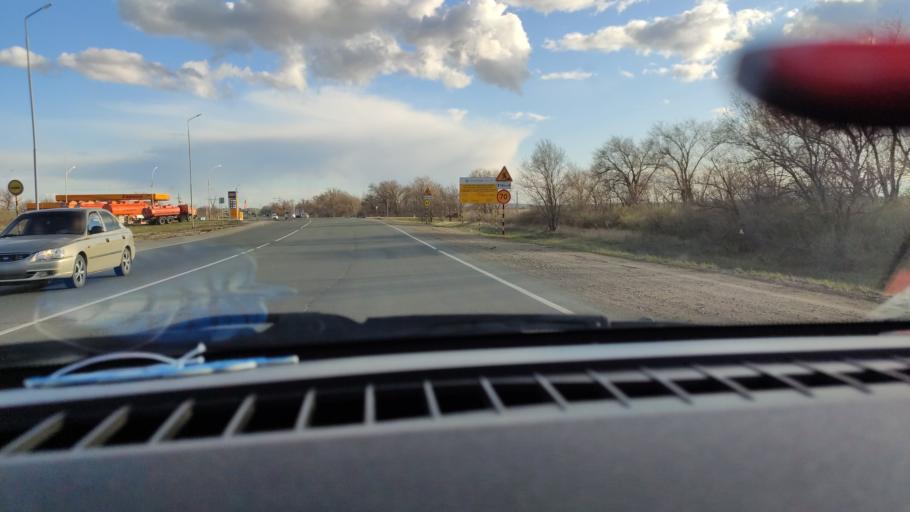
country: RU
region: Saratov
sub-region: Saratovskiy Rayon
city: Saratov
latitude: 51.6782
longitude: 46.0011
